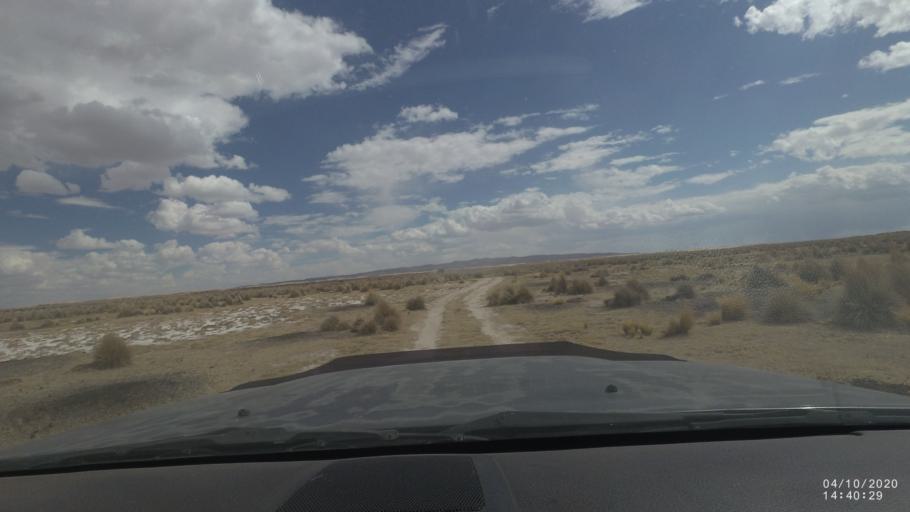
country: BO
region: Oruro
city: Poopo
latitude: -18.6795
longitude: -67.4904
